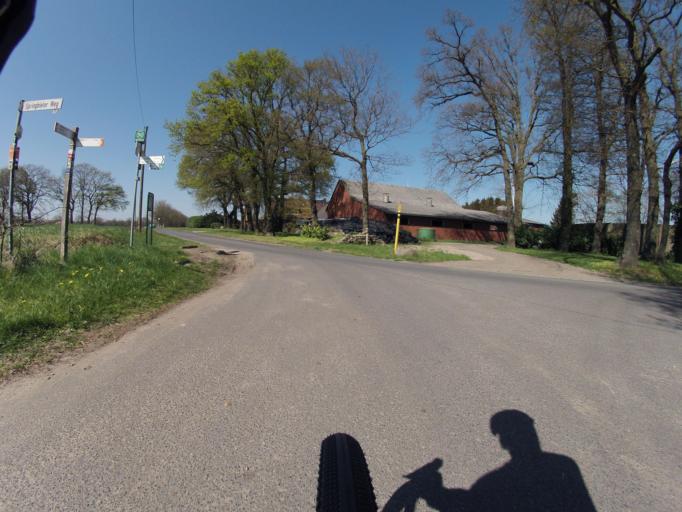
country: NL
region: Overijssel
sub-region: Gemeente Losser
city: Losser
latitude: 52.2954
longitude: 7.0524
